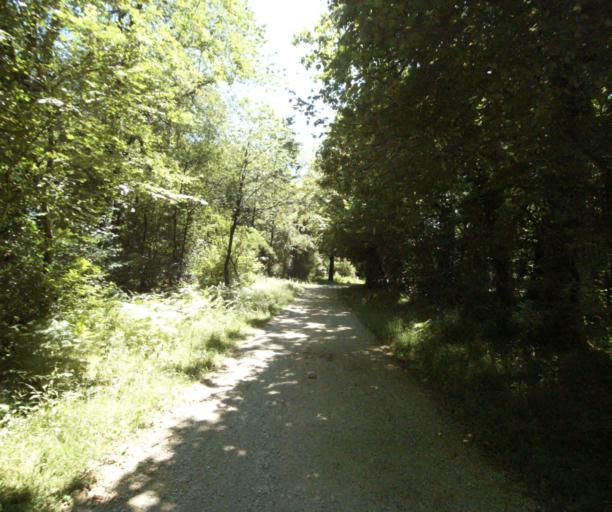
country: FR
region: Midi-Pyrenees
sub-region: Departement du Tarn
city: Dourgne
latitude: 43.4208
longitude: 2.1514
